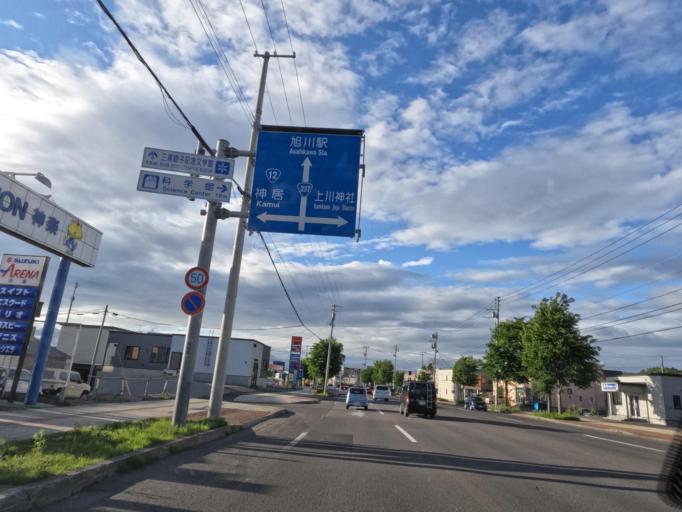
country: JP
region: Hokkaido
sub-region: Asahikawa-shi
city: Asahikawa
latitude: 43.7467
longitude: 142.3578
